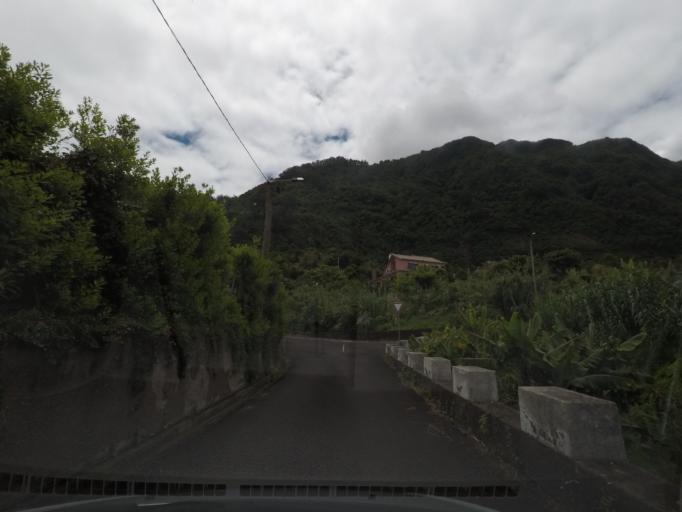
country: PT
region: Madeira
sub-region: Santana
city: Santana
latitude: 32.8276
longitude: -16.9502
